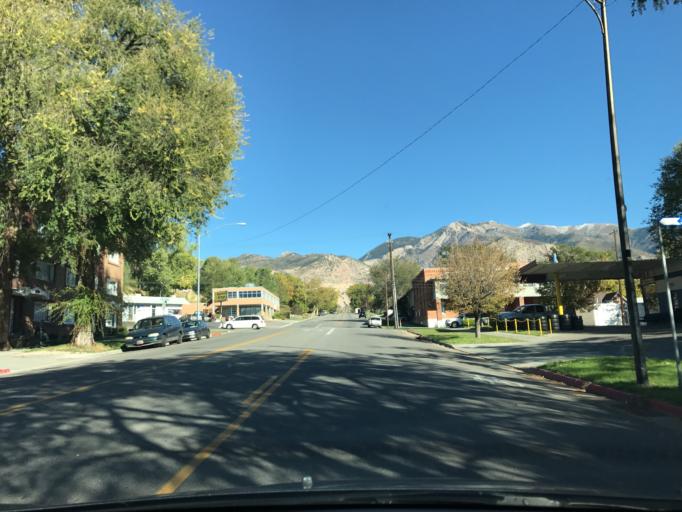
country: US
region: Utah
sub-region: Weber County
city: Ogden
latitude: 41.2185
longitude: -111.9686
